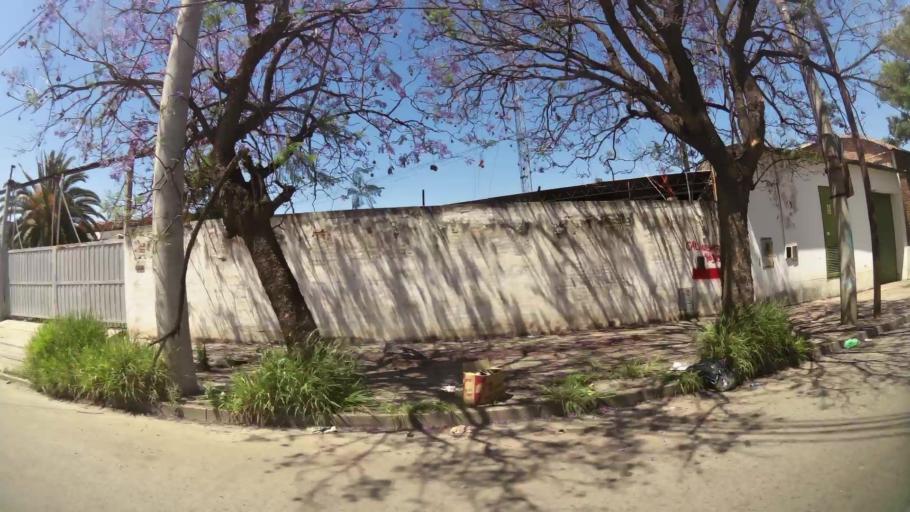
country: AR
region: Cordoba
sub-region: Departamento de Capital
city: Cordoba
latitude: -31.4412
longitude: -64.1255
